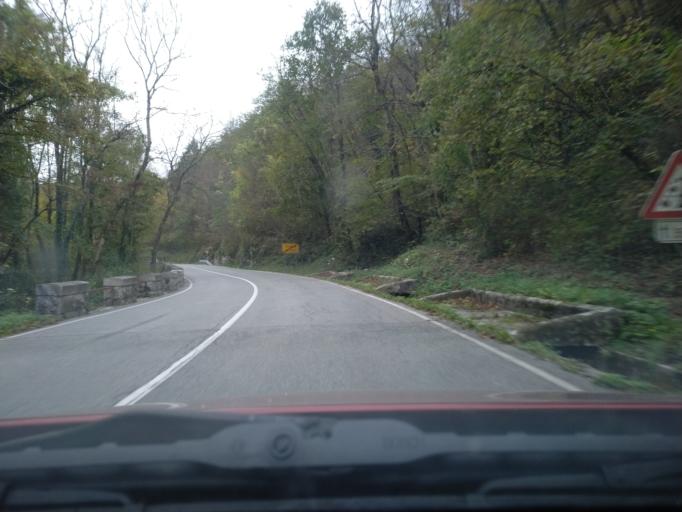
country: SI
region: Kobarid
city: Kobarid
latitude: 46.2784
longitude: 13.5549
